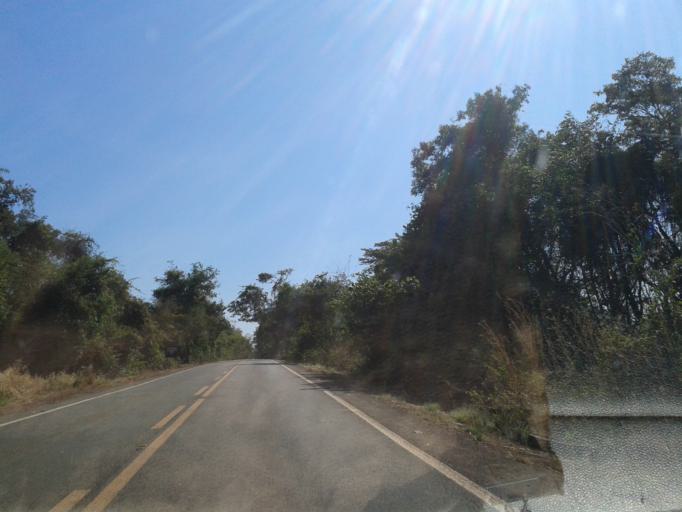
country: BR
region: Goias
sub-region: Crixas
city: Crixas
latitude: -13.9777
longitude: -50.3222
